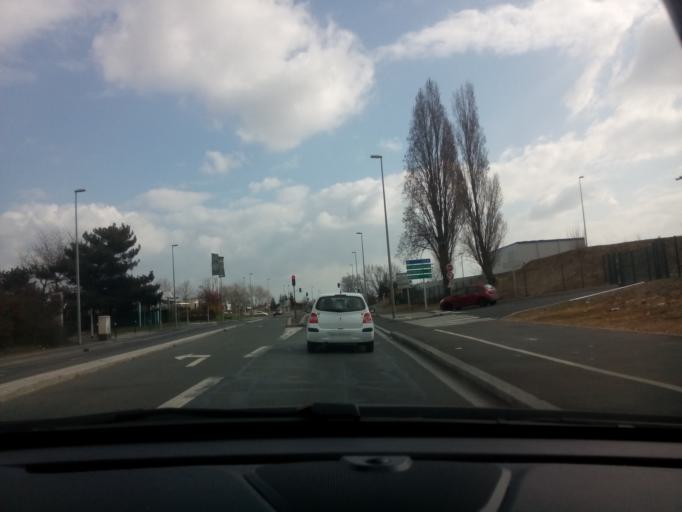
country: FR
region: Ile-de-France
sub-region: Departement du Val-de-Marne
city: Chevilly-Larue
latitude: 48.7567
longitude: 2.3454
